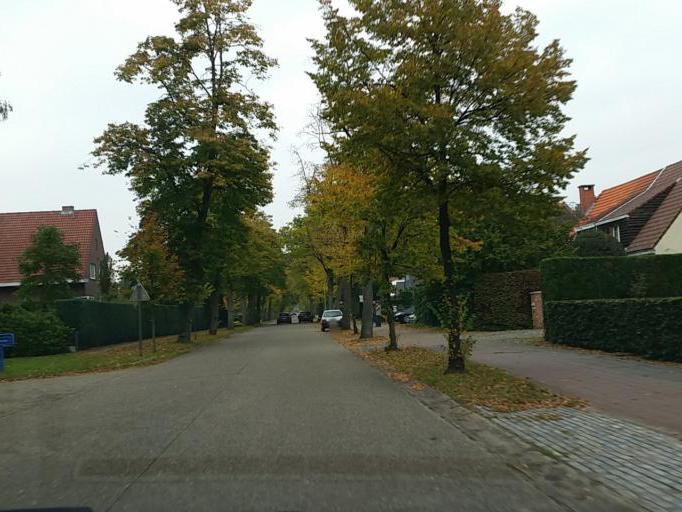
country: BE
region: Flanders
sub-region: Provincie Antwerpen
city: Brasschaat
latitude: 51.3109
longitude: 4.5072
